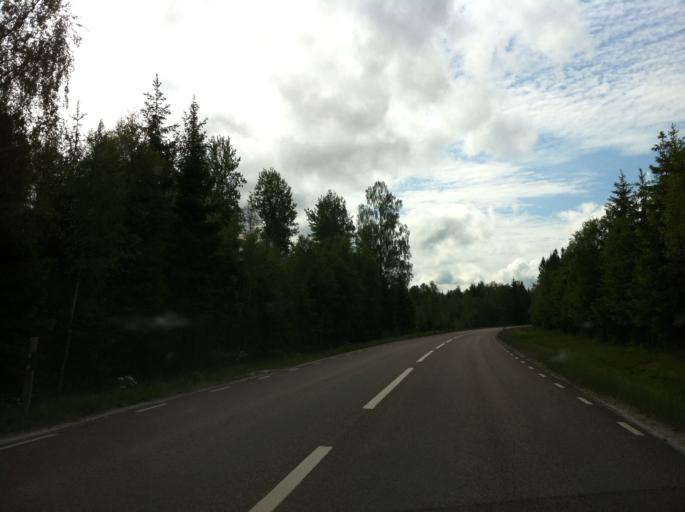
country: SE
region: Vaermland
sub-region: Sunne Kommun
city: Sunne
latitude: 59.7090
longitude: 13.1479
